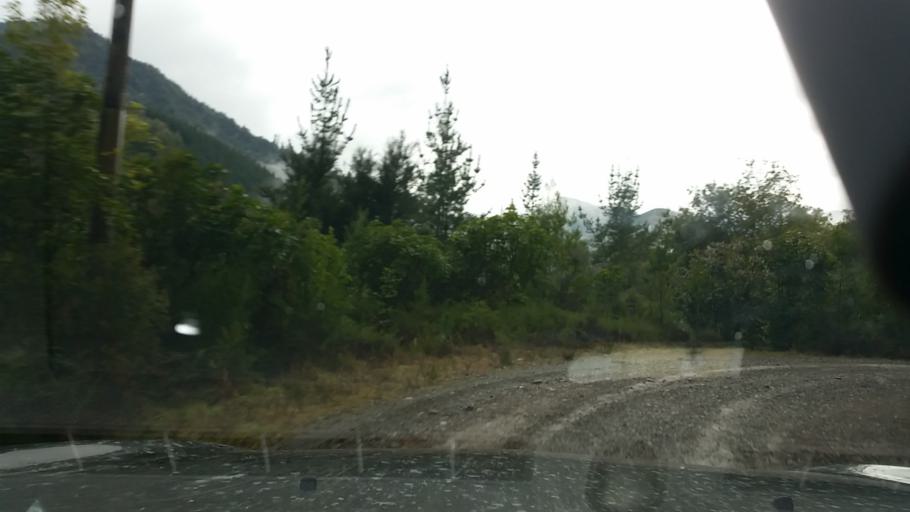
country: NZ
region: Nelson
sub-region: Nelson City
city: Nelson
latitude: -41.3622
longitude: 173.6079
